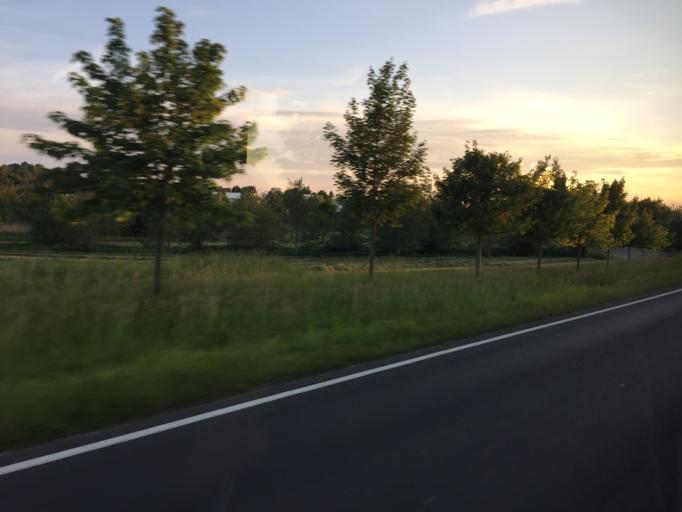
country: DE
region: Saxony
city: Reichenbach
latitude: 51.1501
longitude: 14.7991
